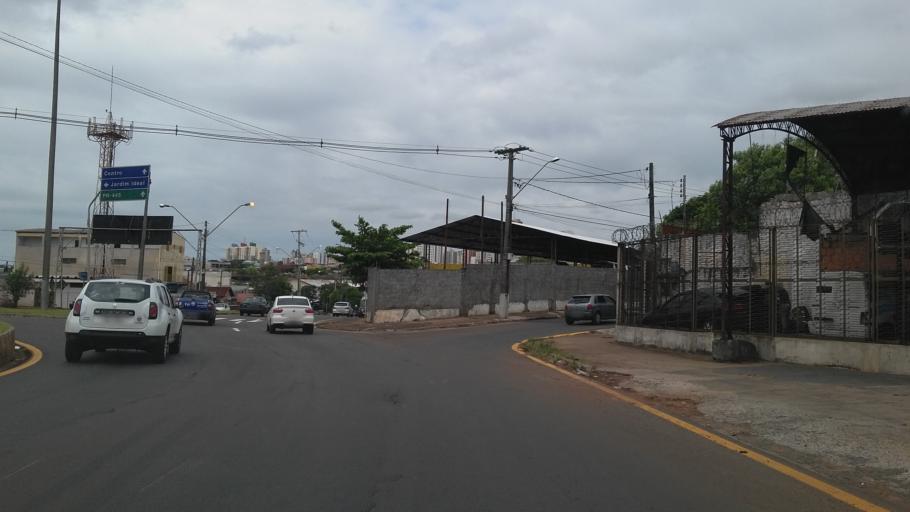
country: BR
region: Parana
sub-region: Londrina
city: Londrina
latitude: -23.3035
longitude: -51.1460
